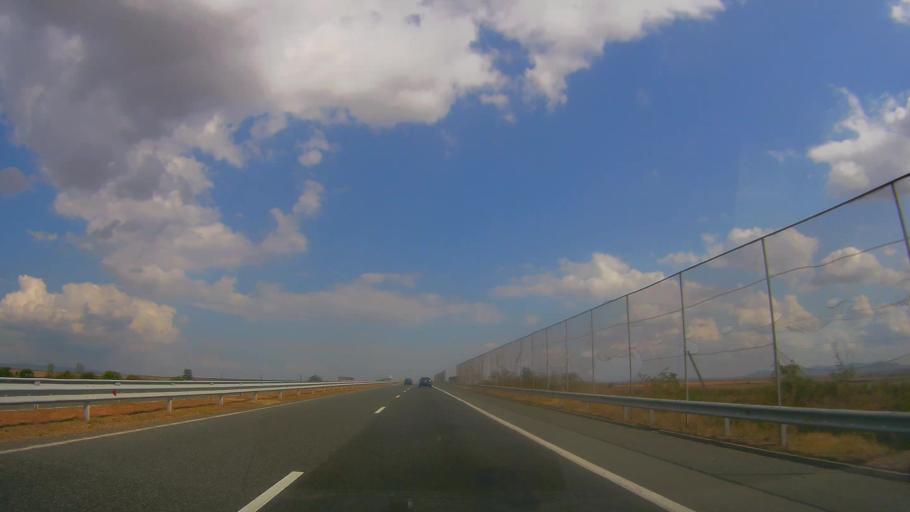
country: BG
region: Yambol
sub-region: Obshtina Yambol
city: Yambol
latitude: 42.5561
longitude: 26.5270
